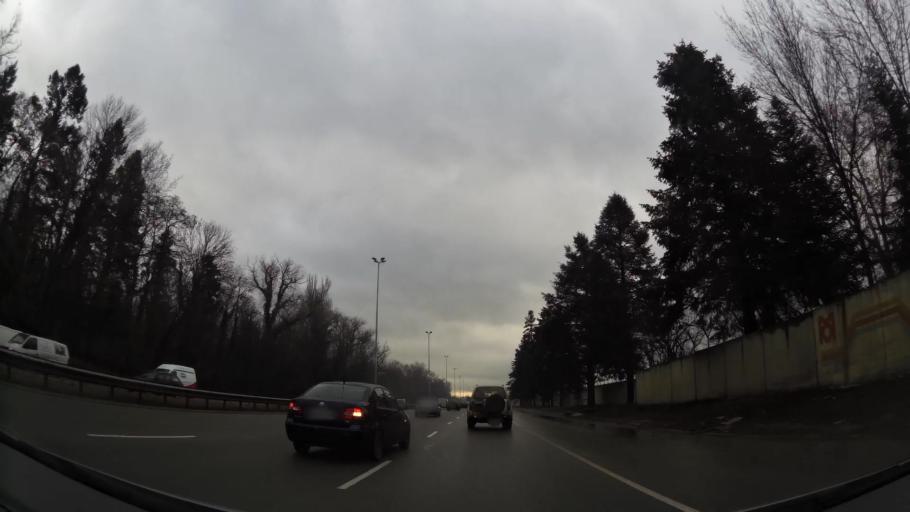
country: BG
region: Sofia-Capital
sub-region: Stolichna Obshtina
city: Sofia
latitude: 42.6357
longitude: 23.4284
